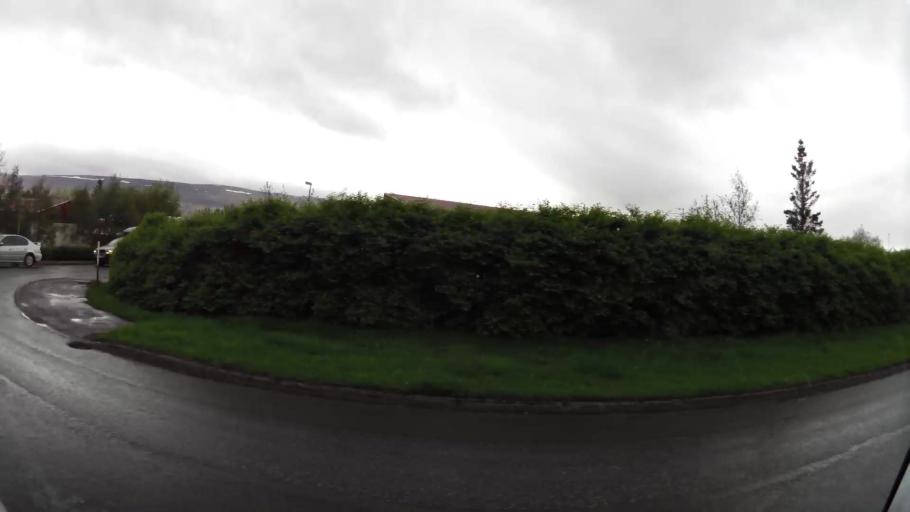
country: IS
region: Northeast
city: Akureyri
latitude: 65.6883
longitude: -18.1361
